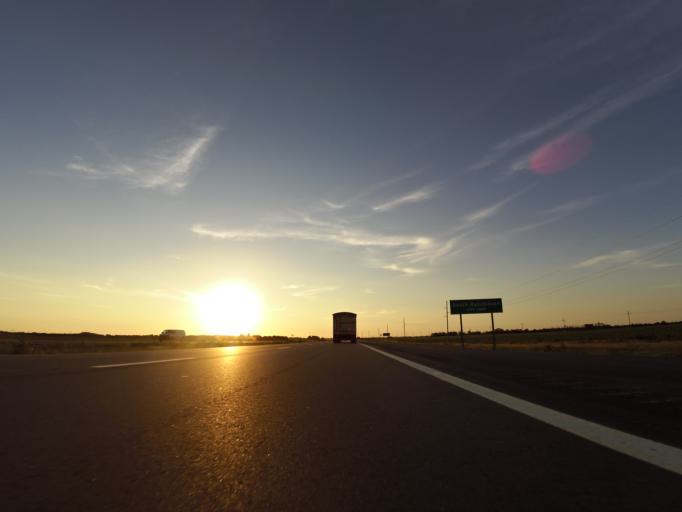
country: US
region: Kansas
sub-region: Reno County
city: South Hutchinson
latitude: 38.0132
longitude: -97.9583
